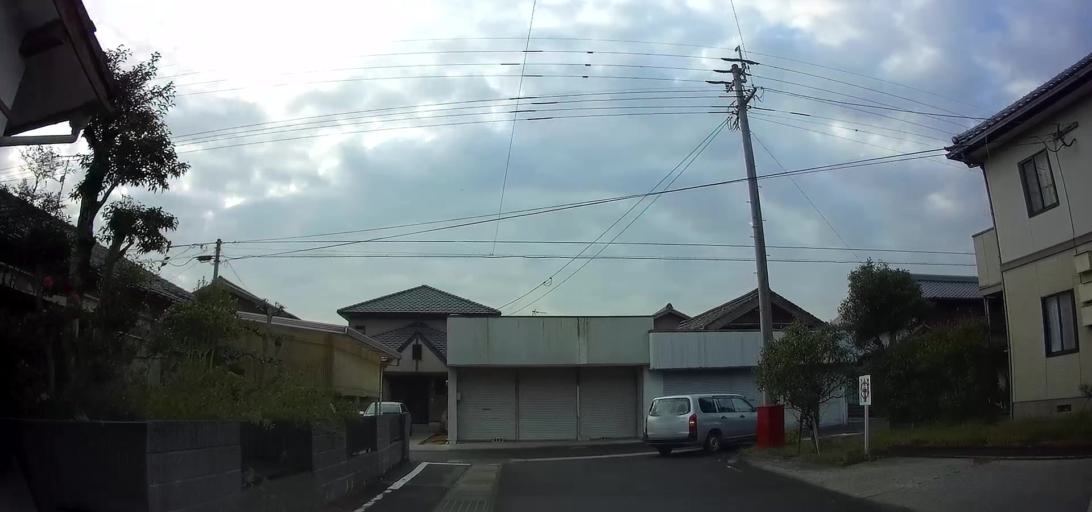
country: JP
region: Nagasaki
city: Shimabara
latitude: 32.6566
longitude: 130.2506
